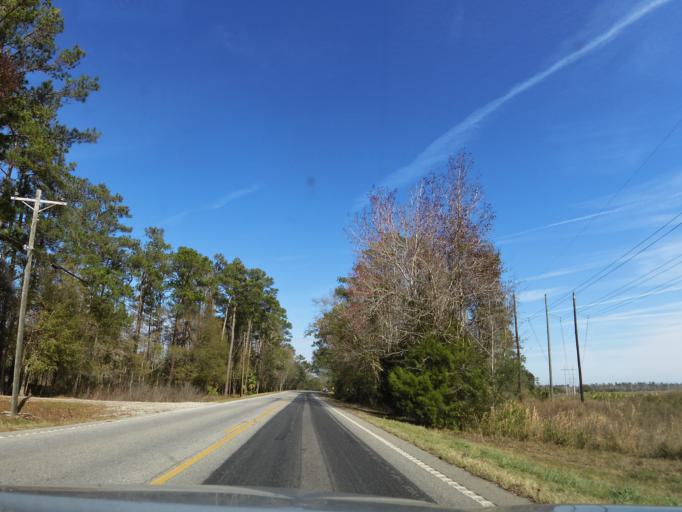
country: US
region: Georgia
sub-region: Glynn County
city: Dock Junction
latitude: 31.2622
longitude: -81.5968
